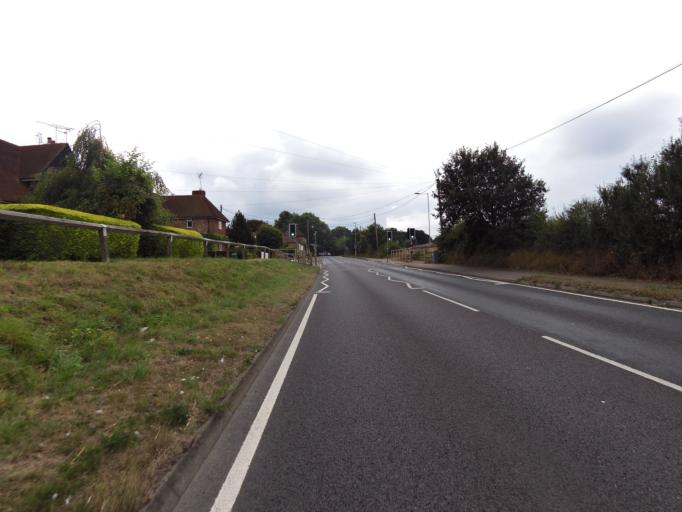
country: GB
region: England
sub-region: Hertfordshire
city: Shenley AV
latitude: 51.7043
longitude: -0.2907
